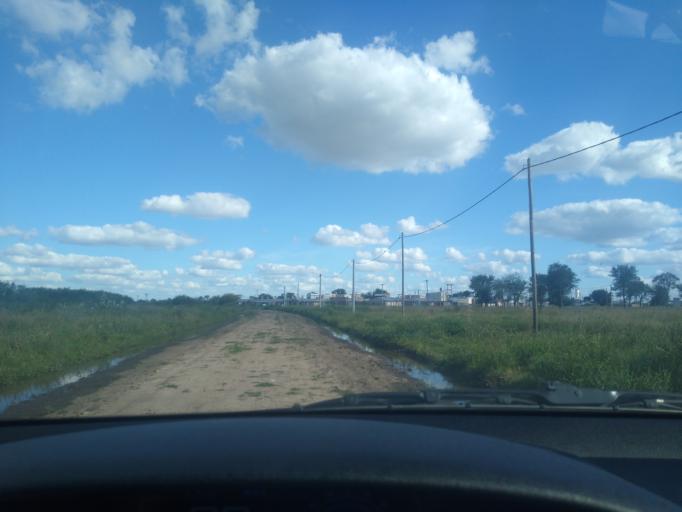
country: AR
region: Chaco
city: Resistencia
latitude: -27.4022
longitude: -58.9601
